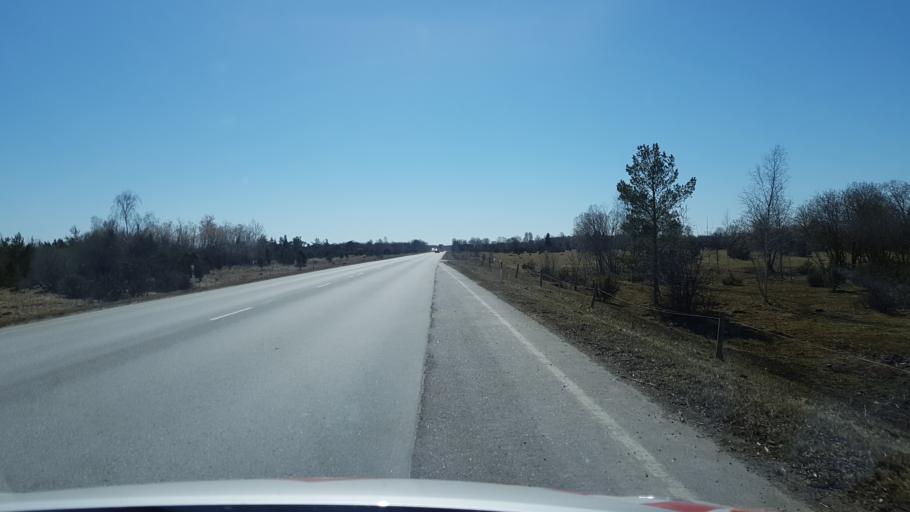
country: EE
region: Laeaene-Virumaa
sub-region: Viru-Nigula vald
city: Kunda
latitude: 59.4780
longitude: 26.4860
